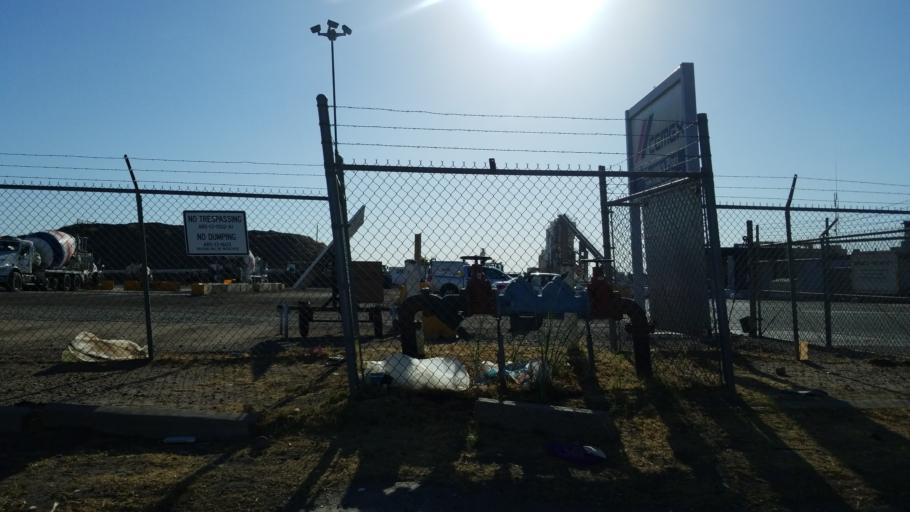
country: US
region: Arizona
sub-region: Maricopa County
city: Phoenix
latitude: 33.4150
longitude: -112.0997
